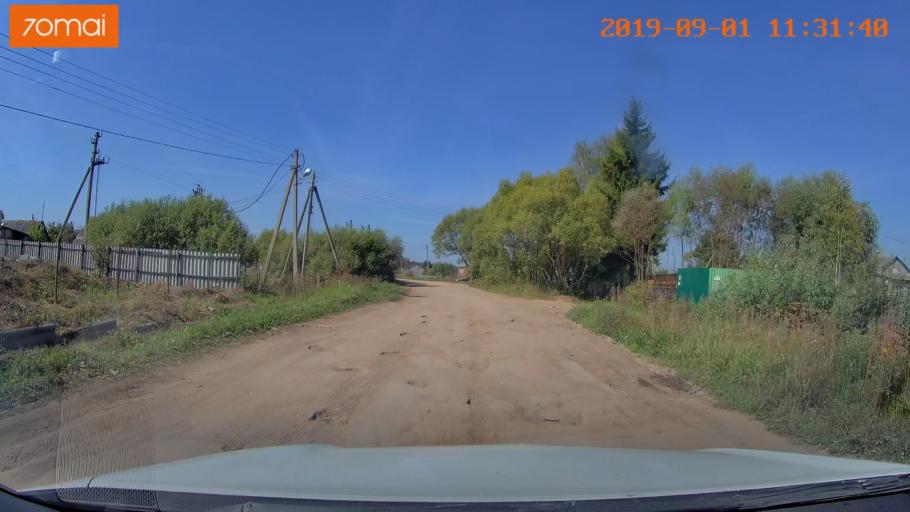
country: RU
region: Kaluga
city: Detchino
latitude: 54.8351
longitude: 36.3369
